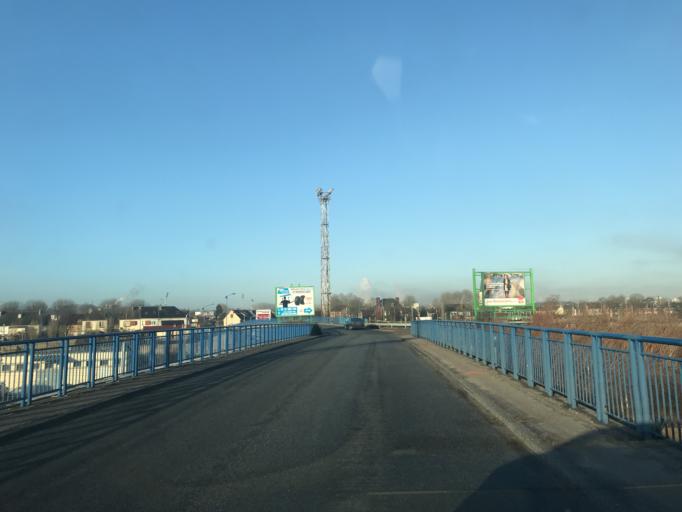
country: FR
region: Haute-Normandie
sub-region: Departement de la Seine-Maritime
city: Sotteville-les-Rouen
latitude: 49.4049
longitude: 1.1064
